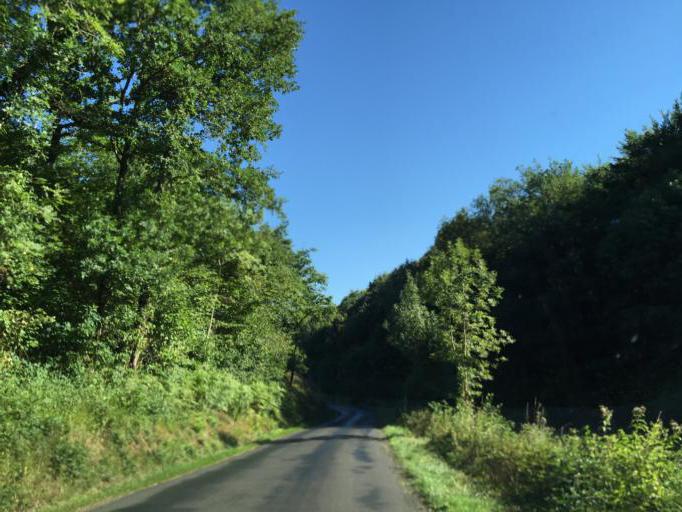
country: FR
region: Midi-Pyrenees
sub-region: Departement de l'Aveyron
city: Laissac
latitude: 44.3687
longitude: 2.7974
